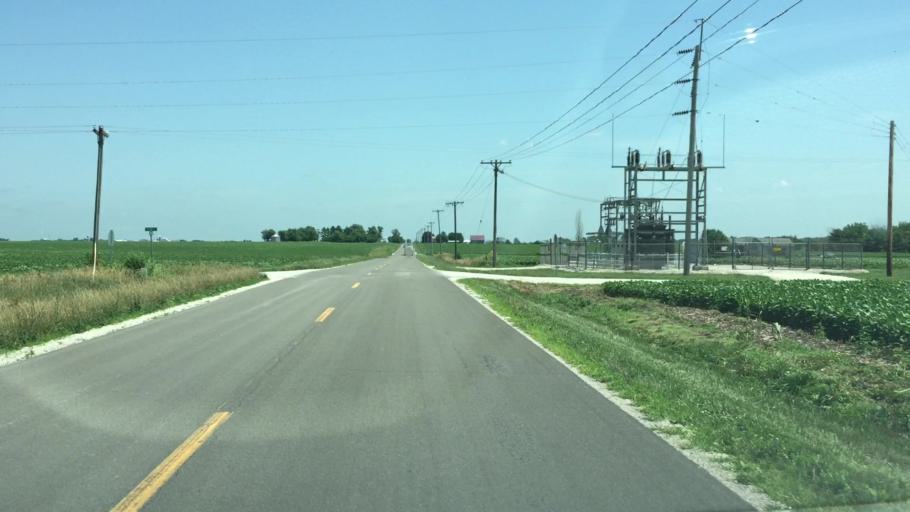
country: US
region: Illinois
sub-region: Hancock County
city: Carthage
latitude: 40.3280
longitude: -91.1815
